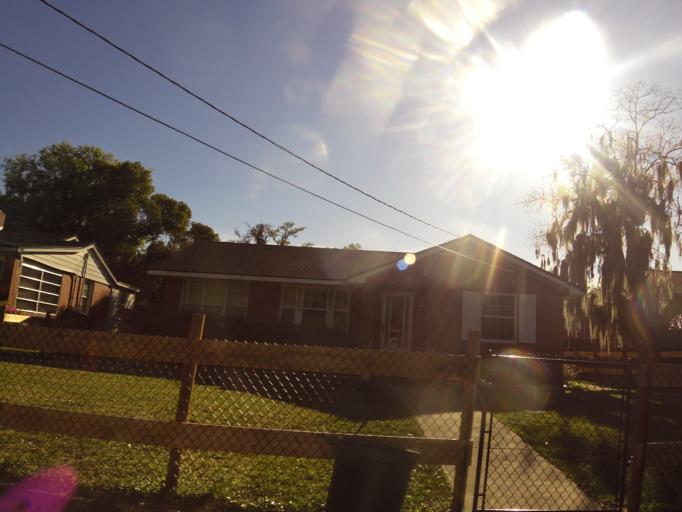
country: US
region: Florida
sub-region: Duval County
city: Jacksonville
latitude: 30.3864
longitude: -81.6538
